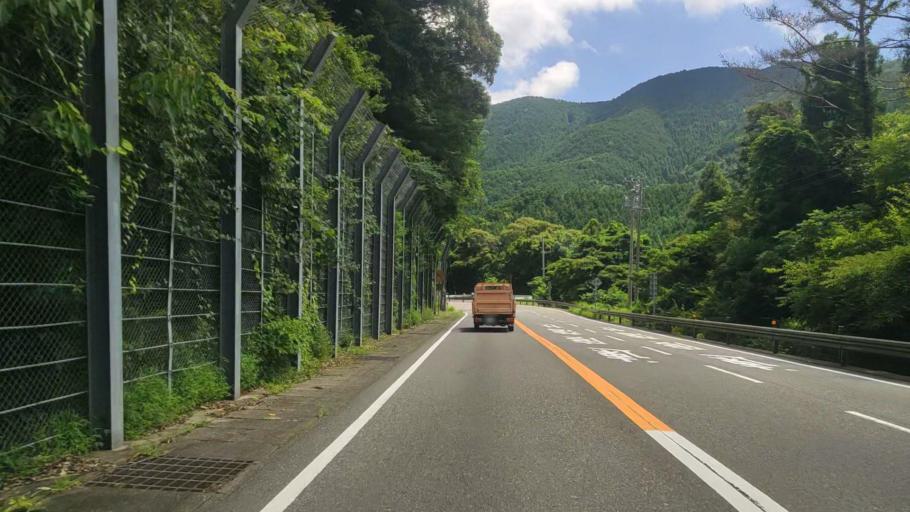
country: JP
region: Mie
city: Owase
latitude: 33.9215
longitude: 136.1009
